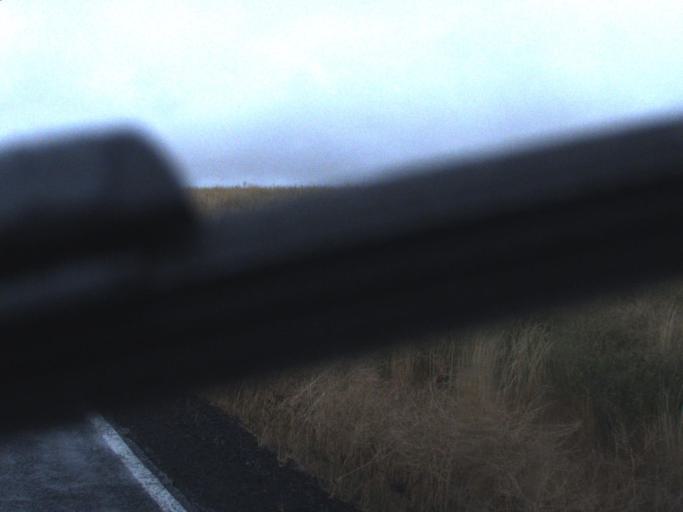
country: US
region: Washington
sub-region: Lincoln County
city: Davenport
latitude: 47.3437
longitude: -118.0084
